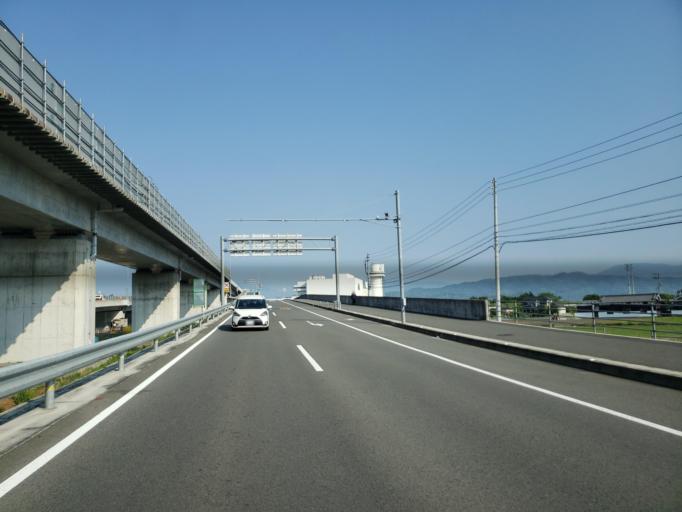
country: JP
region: Ehime
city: Masaki-cho
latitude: 33.8100
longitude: 132.7350
